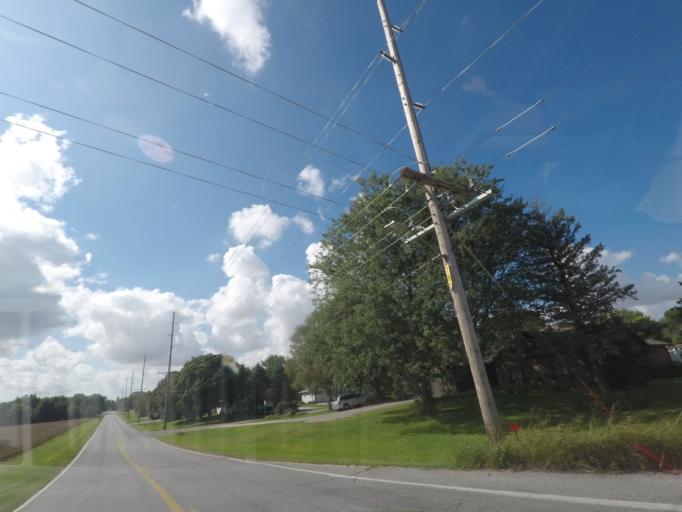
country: US
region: Iowa
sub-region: Story County
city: Nevada
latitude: 42.0224
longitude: -93.3192
